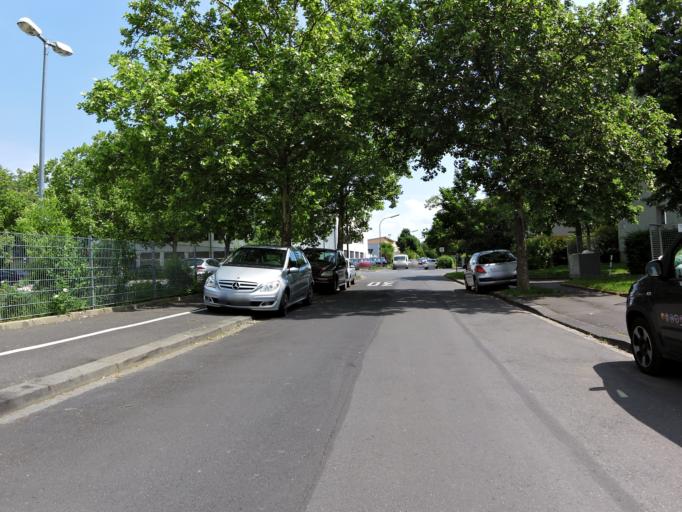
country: DE
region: Bavaria
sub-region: Regierungsbezirk Unterfranken
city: Hochberg
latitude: 49.7954
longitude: 9.9004
